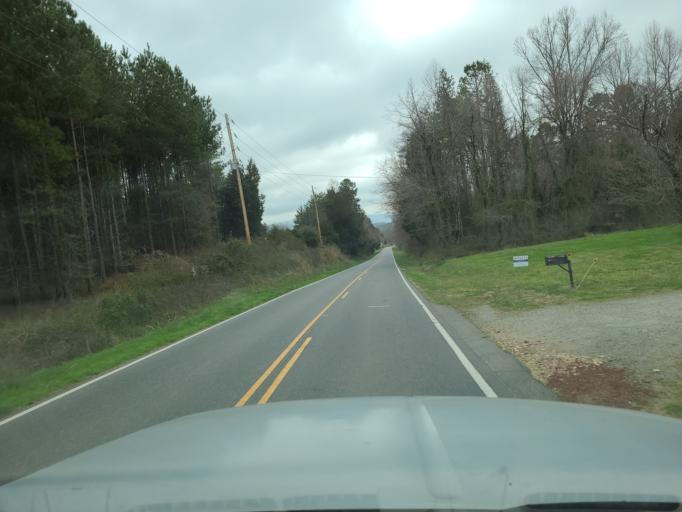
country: US
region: North Carolina
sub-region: Cleveland County
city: Shelby
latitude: 35.4415
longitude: -81.6439
